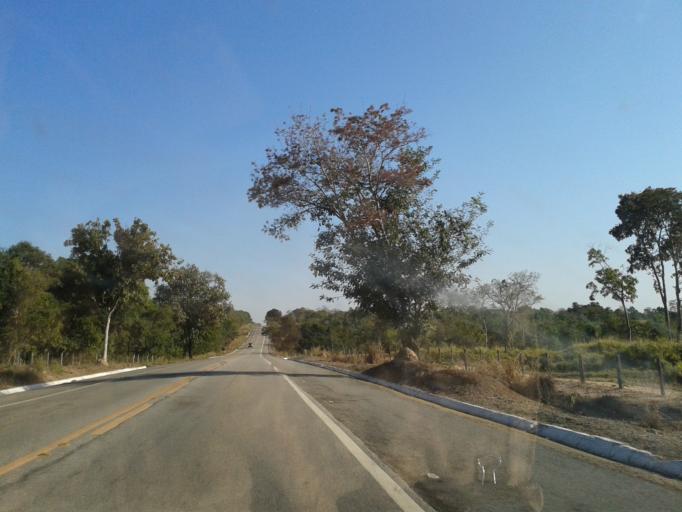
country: BR
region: Goias
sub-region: Mozarlandia
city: Mozarlandia
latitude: -15.2163
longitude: -50.5318
